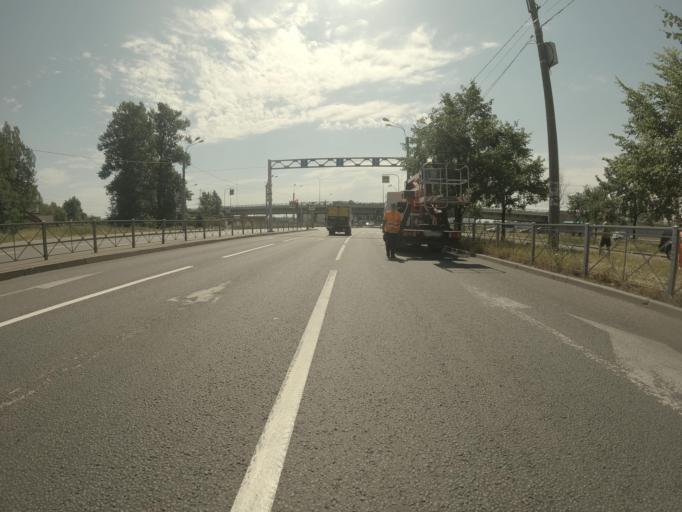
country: RU
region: St.-Petersburg
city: Krasnogvargeisky
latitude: 59.9465
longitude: 30.5047
